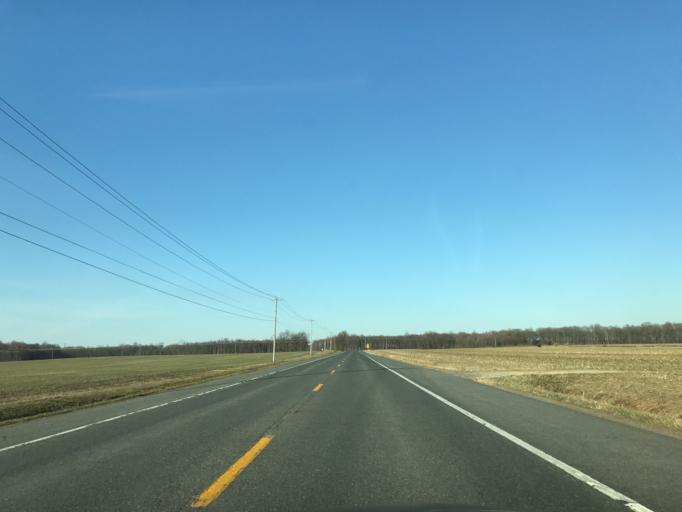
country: US
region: Maryland
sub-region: Queen Anne's County
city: Kingstown
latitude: 39.1594
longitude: -75.8638
